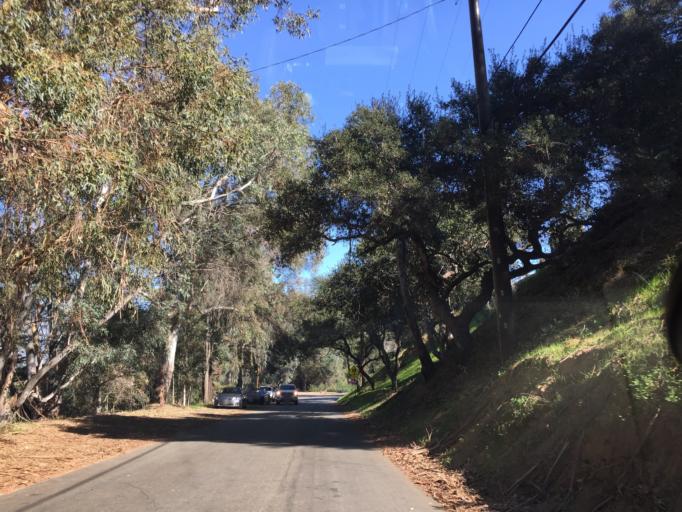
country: US
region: California
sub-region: Santa Barbara County
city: Goleta
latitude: 34.4346
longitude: -119.7706
